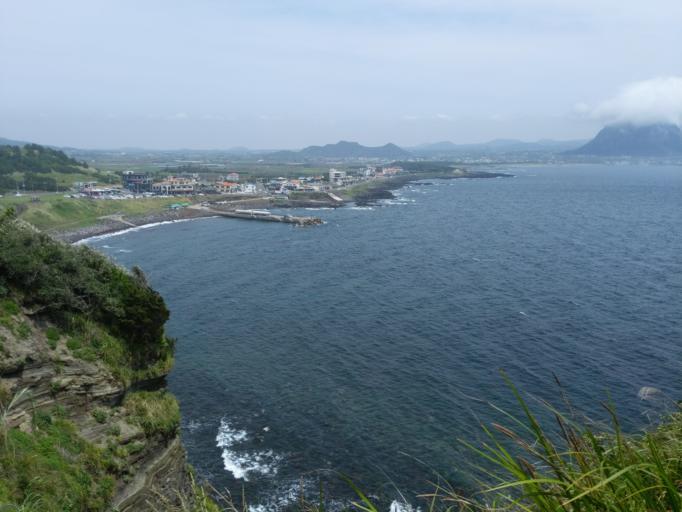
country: KR
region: Jeju-do
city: Gaigeturi
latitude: 33.2027
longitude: 126.2919
